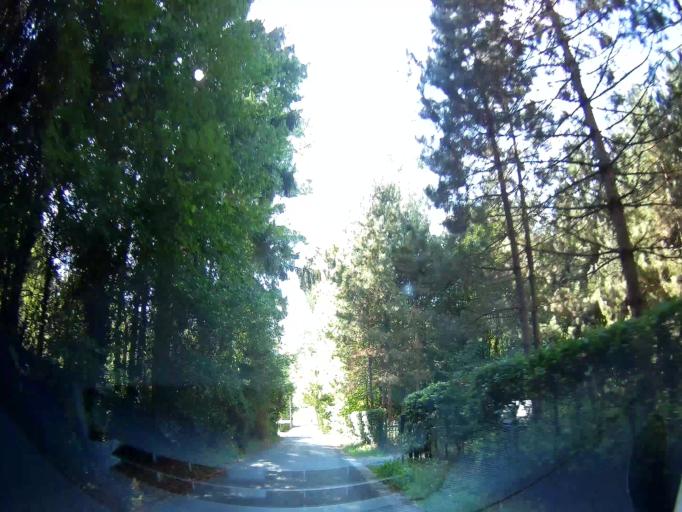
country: BE
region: Wallonia
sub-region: Province de Namur
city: Onhaye
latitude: 50.2961
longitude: 4.7756
